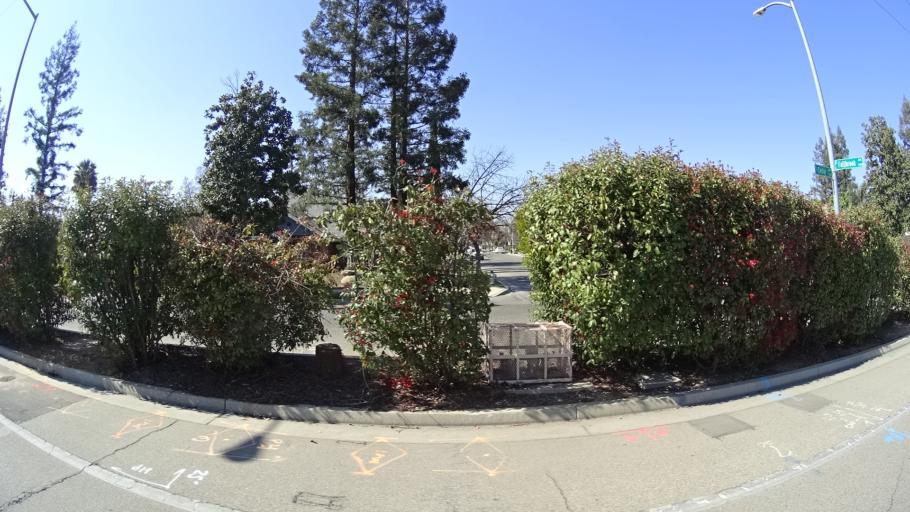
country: US
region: California
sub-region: Fresno County
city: Clovis
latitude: 36.8494
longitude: -119.7569
